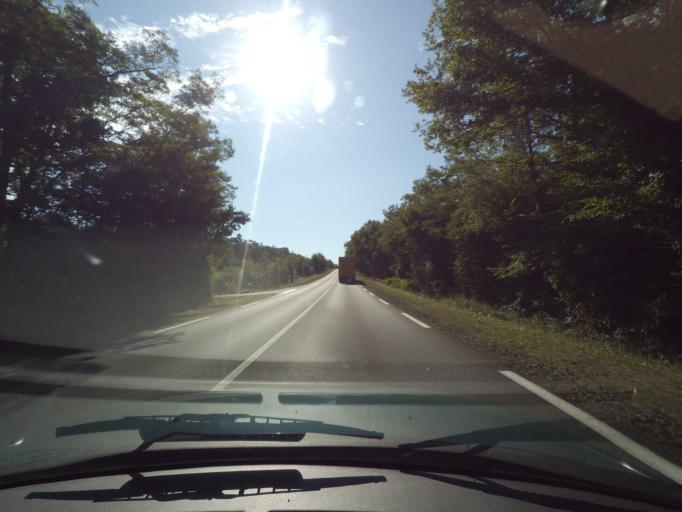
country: FR
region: Poitou-Charentes
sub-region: Departement de la Vienne
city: Terce
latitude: 46.4281
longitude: 0.6179
